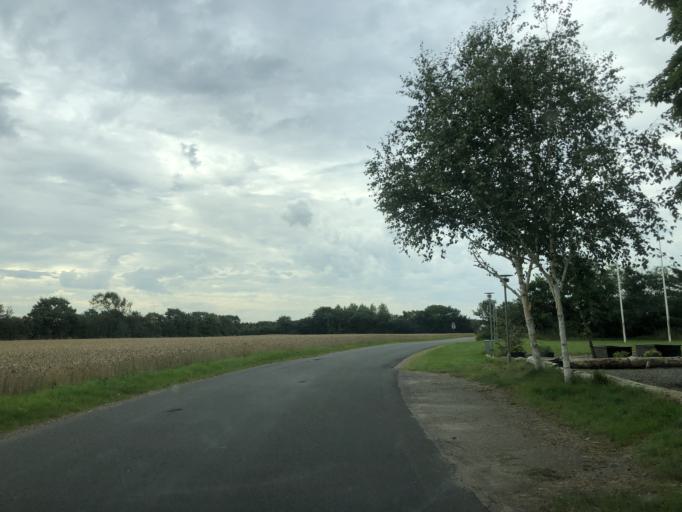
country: DK
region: Central Jutland
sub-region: Holstebro Kommune
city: Holstebro
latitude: 56.3794
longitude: 8.5232
